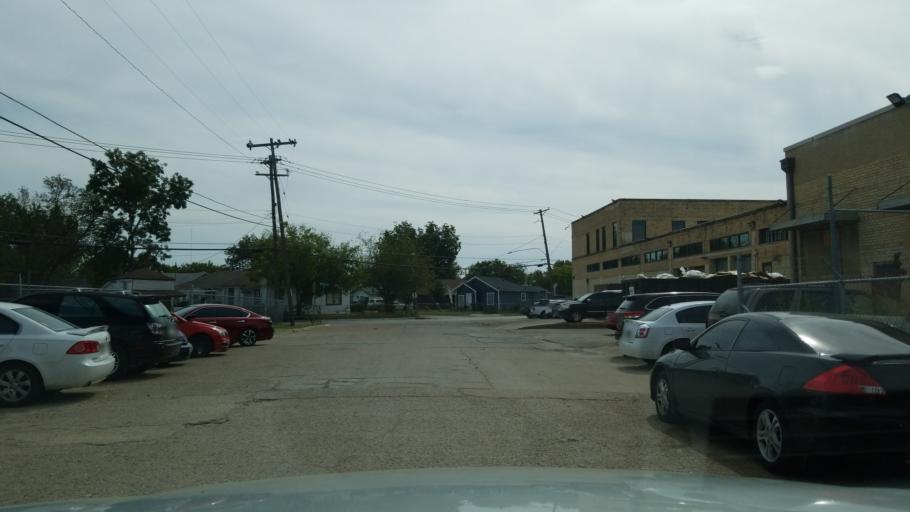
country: US
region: Texas
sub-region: Dallas County
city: Dallas
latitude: 32.7853
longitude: -96.7450
